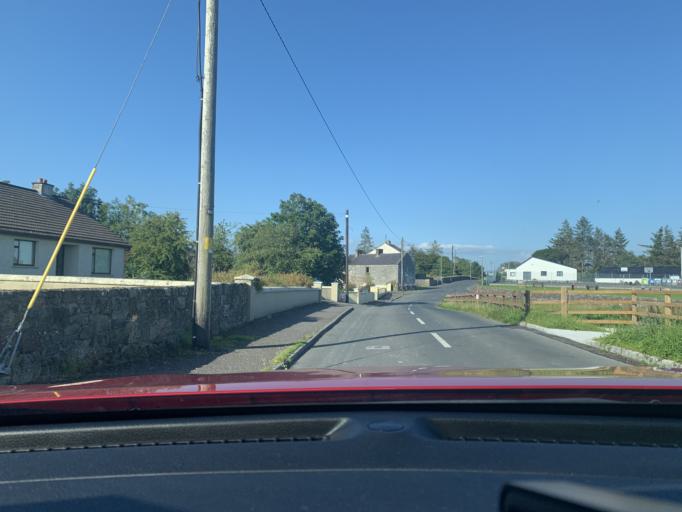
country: IE
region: Connaught
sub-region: Sligo
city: Tobercurry
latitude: 54.1001
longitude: -8.7788
